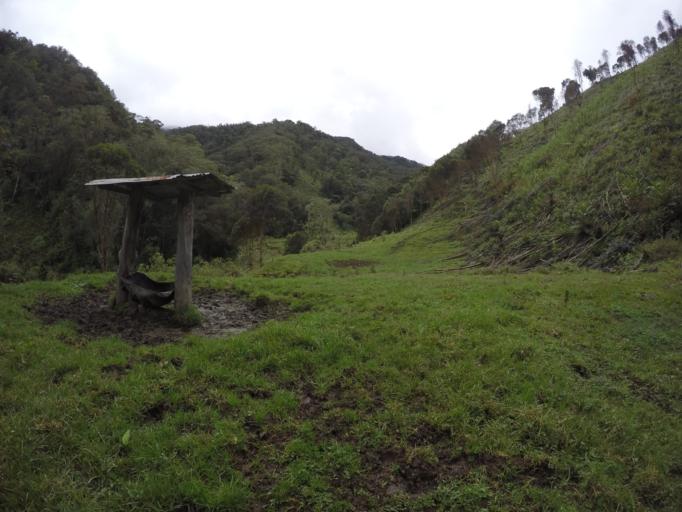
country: CO
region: Tolima
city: Cajamarca
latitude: 4.5264
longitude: -75.3591
